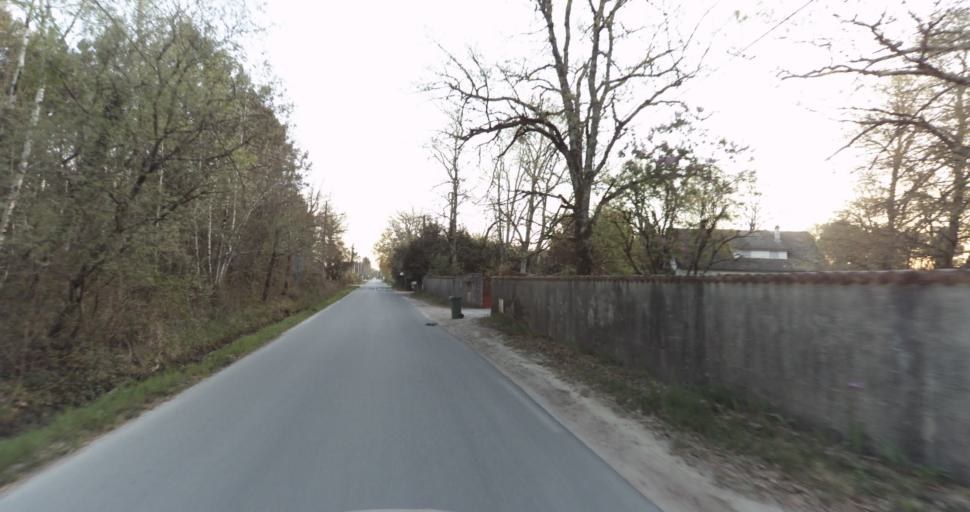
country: FR
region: Aquitaine
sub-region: Departement de la Gironde
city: Saint-Aubin-de-Medoc
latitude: 44.8058
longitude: -0.7280
